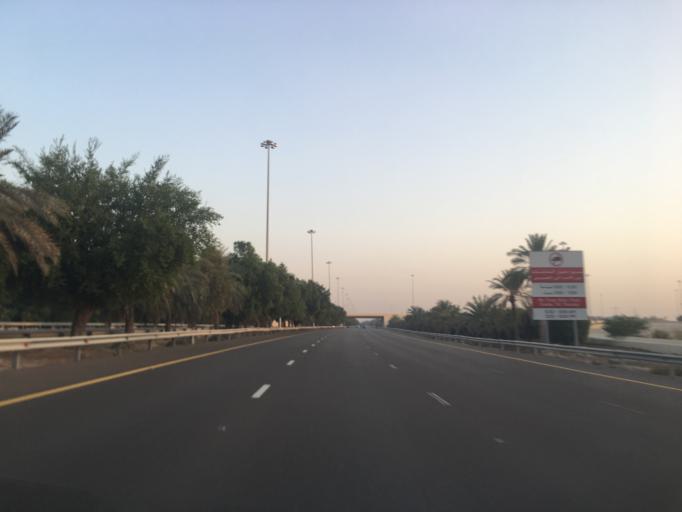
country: AE
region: Abu Dhabi
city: Abu Dhabi
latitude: 24.3487
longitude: 54.5712
